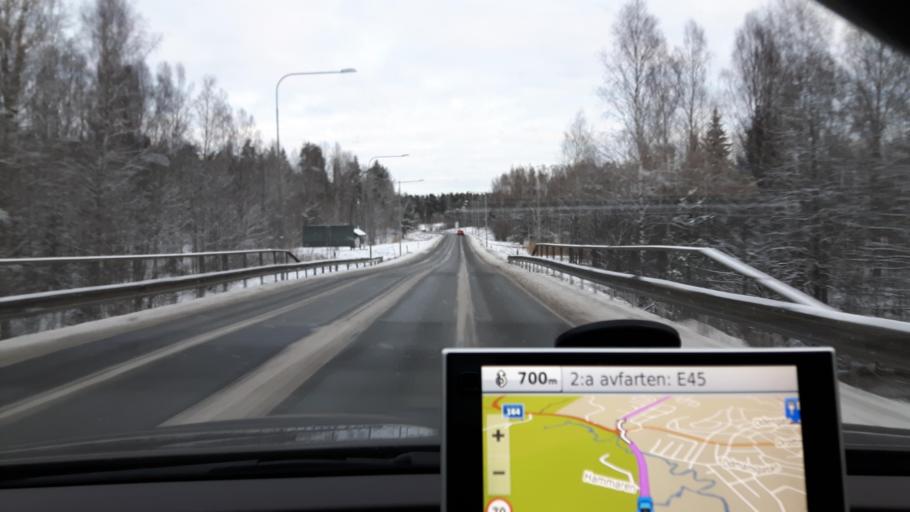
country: SE
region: Vaestra Goetaland
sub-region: Amals Kommun
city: Amal
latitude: 59.0486
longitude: 12.6782
